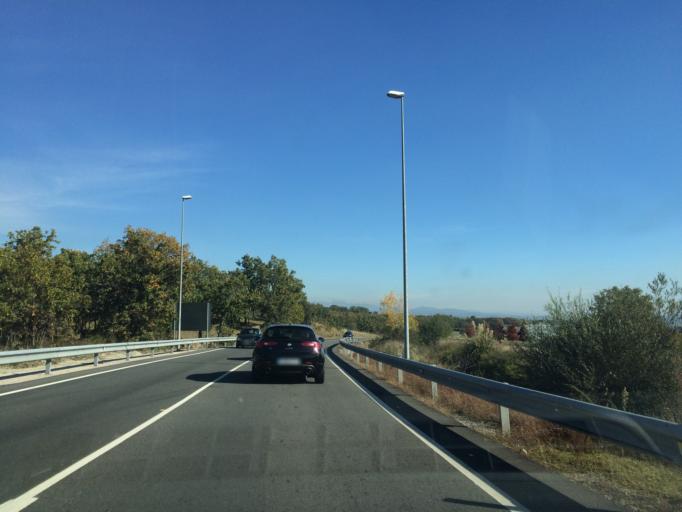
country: ES
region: Madrid
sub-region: Provincia de Madrid
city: Miraflores de la Sierra
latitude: 40.7653
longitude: -3.7472
